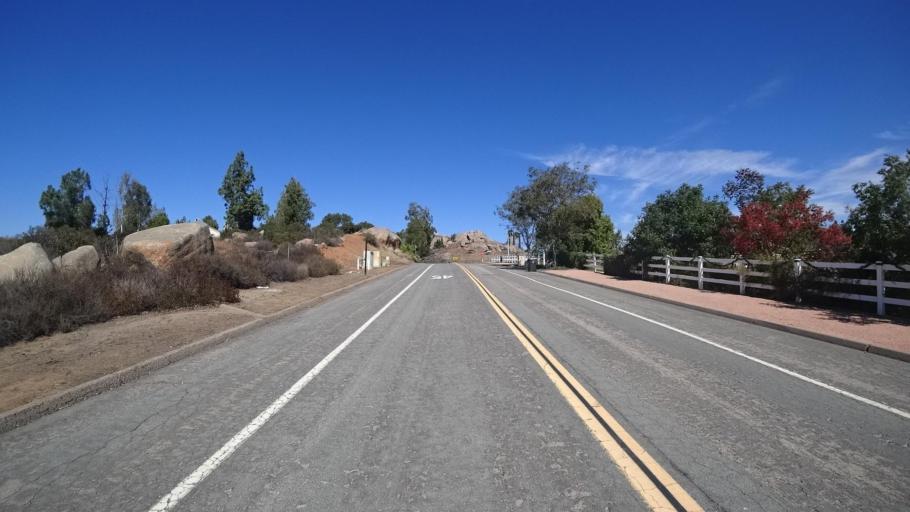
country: US
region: California
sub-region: San Diego County
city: Harbison Canyon
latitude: 32.8748
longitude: -116.8370
